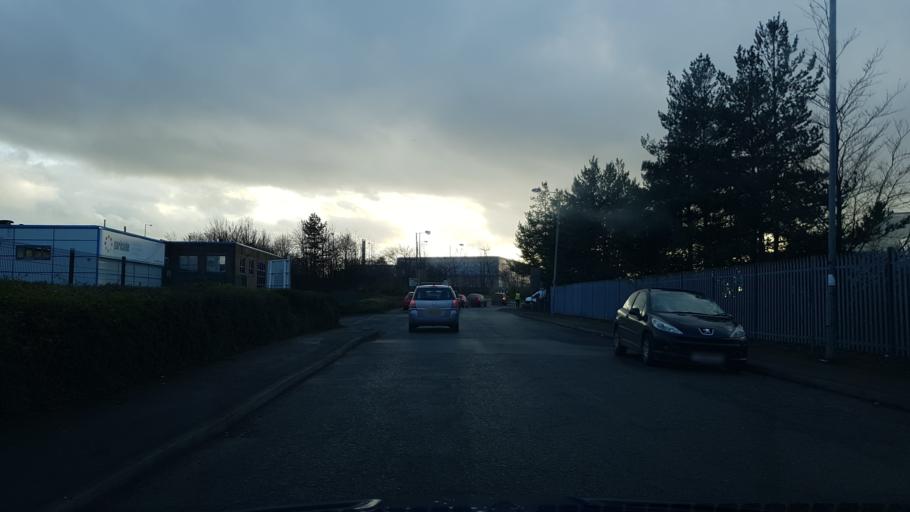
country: GB
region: England
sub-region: City and Borough of Wakefield
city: Normanton
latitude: 53.7017
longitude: -1.3920
